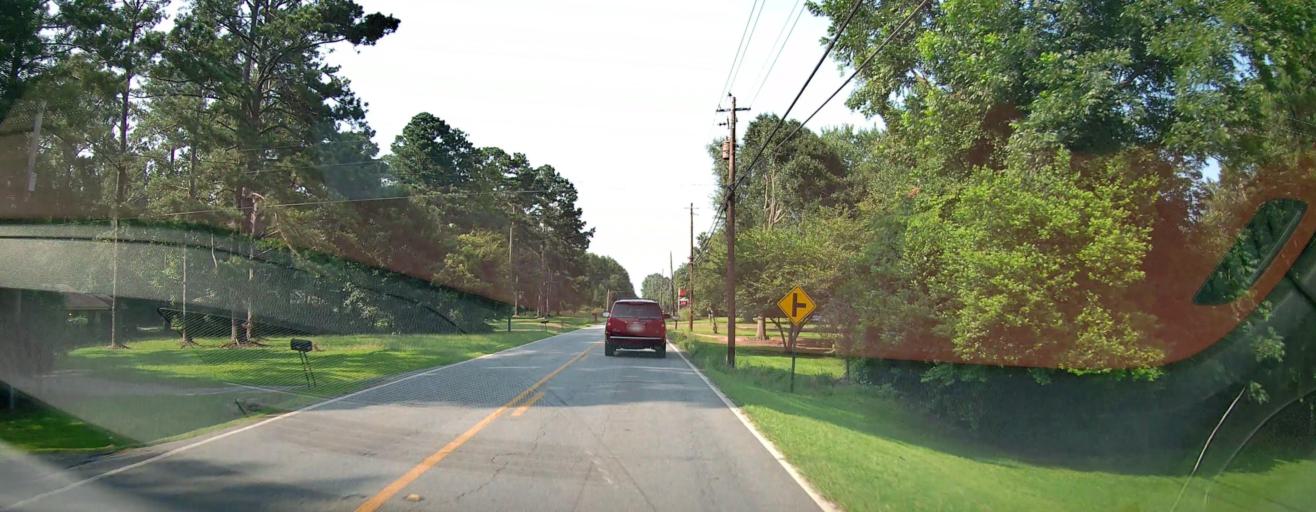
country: US
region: Georgia
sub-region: Houston County
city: Centerville
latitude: 32.7024
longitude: -83.6993
